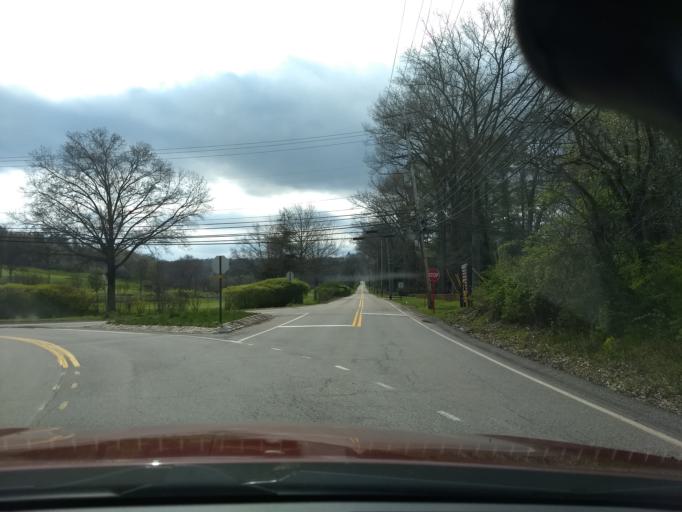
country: US
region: Pennsylvania
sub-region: Allegheny County
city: Fox Chapel
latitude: 40.5281
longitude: -79.8794
